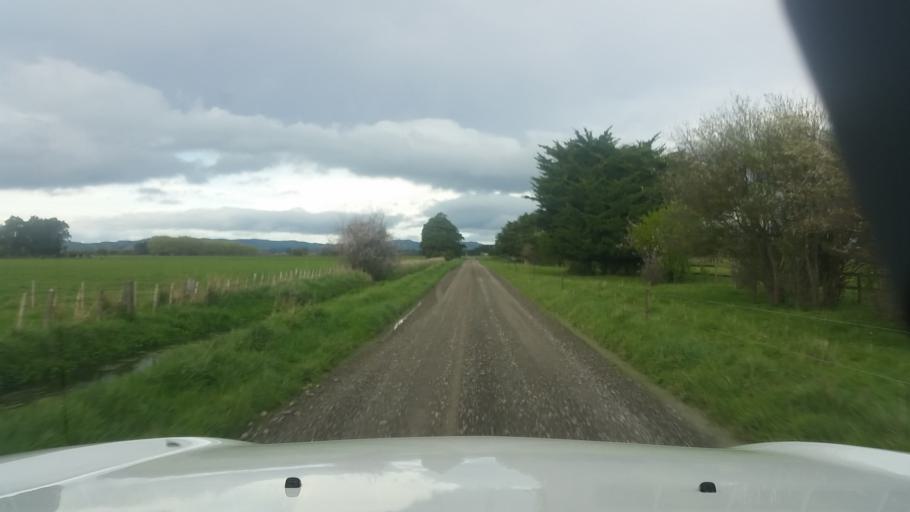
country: NZ
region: Wellington
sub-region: South Wairarapa District
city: Waipawa
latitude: -41.1470
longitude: 175.3841
